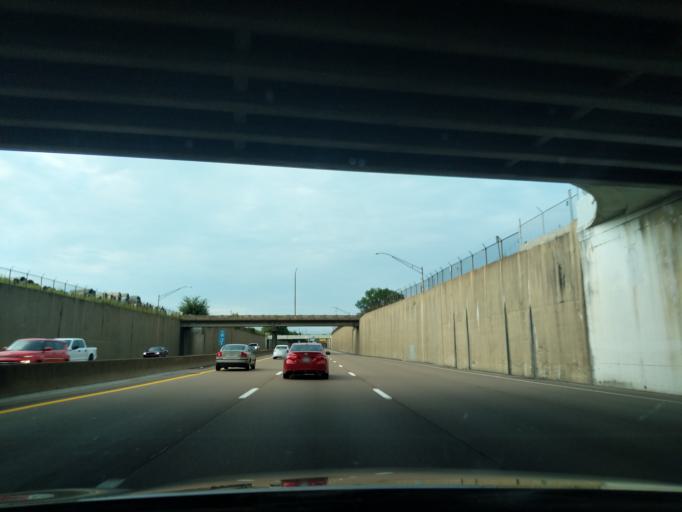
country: US
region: Tennessee
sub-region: Shelby County
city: New South Memphis
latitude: 35.1087
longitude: -90.0750
